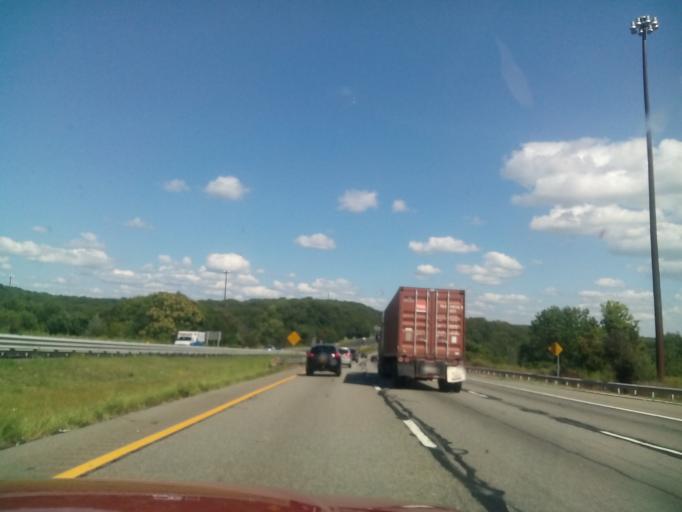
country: US
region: New Jersey
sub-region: Morris County
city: Succasunna
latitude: 40.8926
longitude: -74.6693
